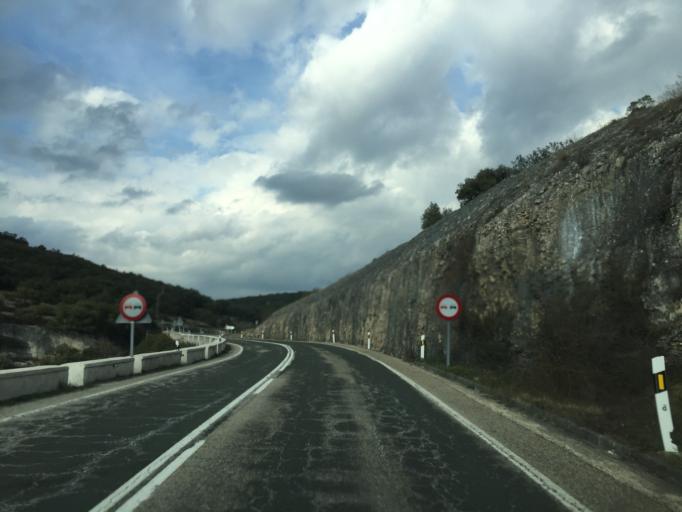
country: ES
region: Cantabria
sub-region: Provincia de Cantabria
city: San Martin de Elines
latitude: 42.8169
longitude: -3.7703
